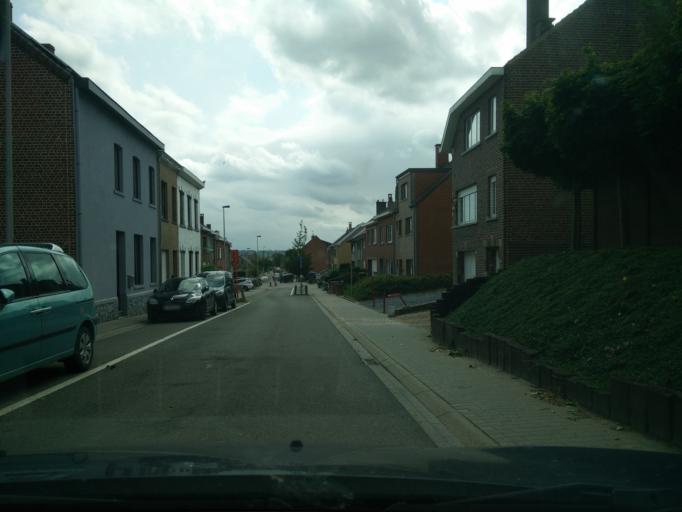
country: BE
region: Wallonia
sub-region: Province du Brabant Wallon
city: Tubize
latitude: 50.7185
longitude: 4.2051
